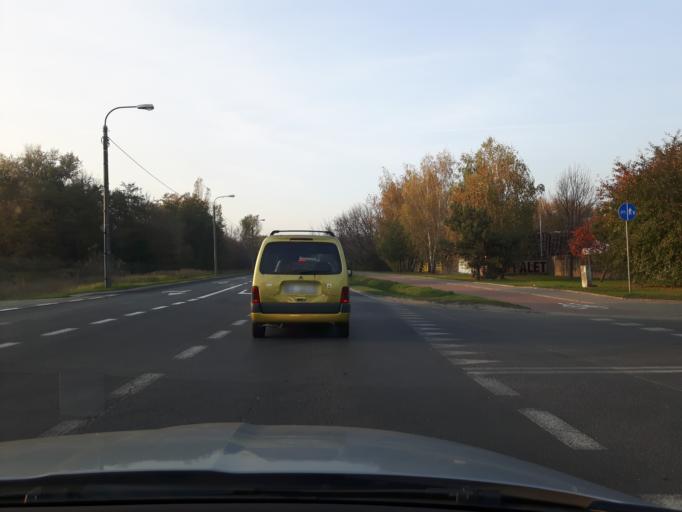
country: PL
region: Masovian Voivodeship
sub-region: Warszawa
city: Praga Poludnie
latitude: 52.2658
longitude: 21.0752
